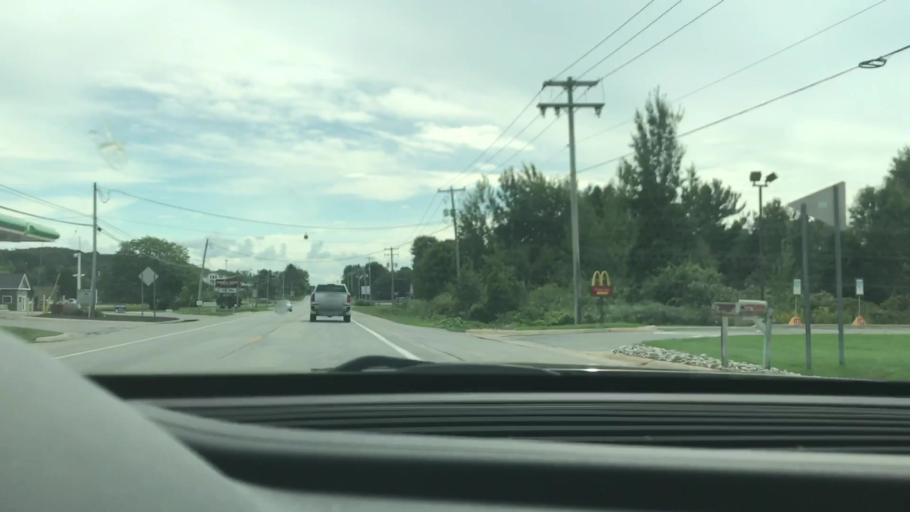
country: US
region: Michigan
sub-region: Antrim County
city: Bellaire
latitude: 44.9737
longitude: -85.1984
